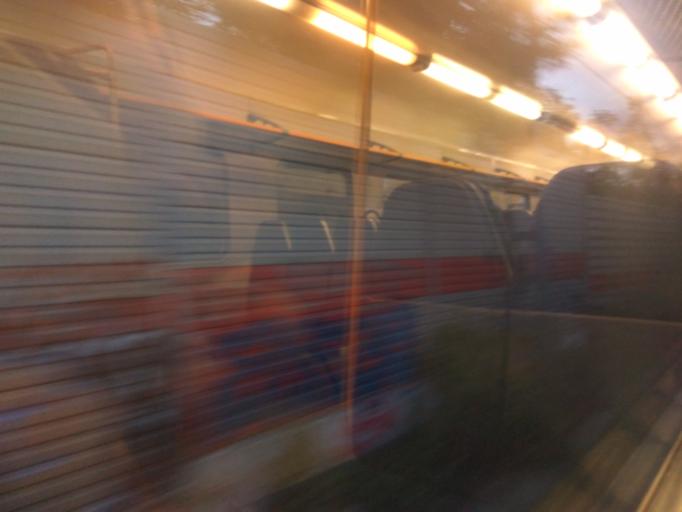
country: RU
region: Moscow
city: Solntsevo
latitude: 55.6502
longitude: 37.3805
